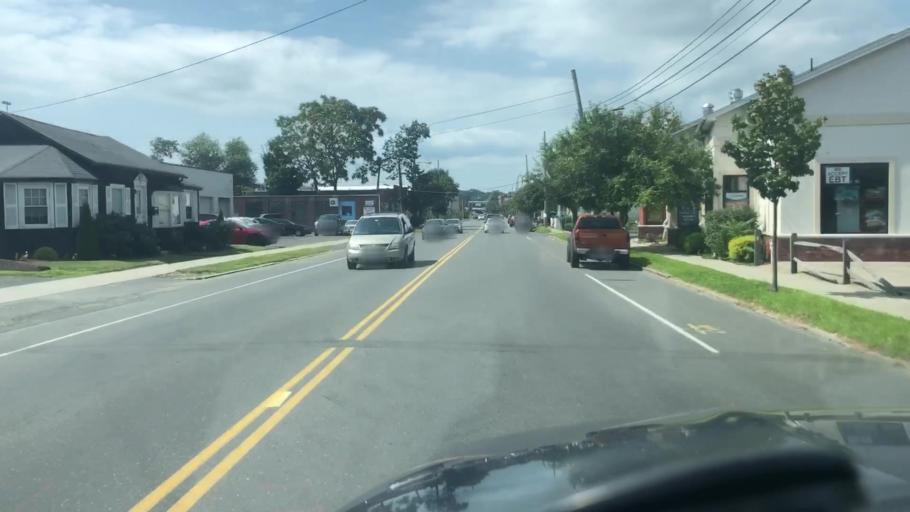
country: US
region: Massachusetts
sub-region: Hampden County
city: West Springfield
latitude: 42.0984
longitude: -72.6080
